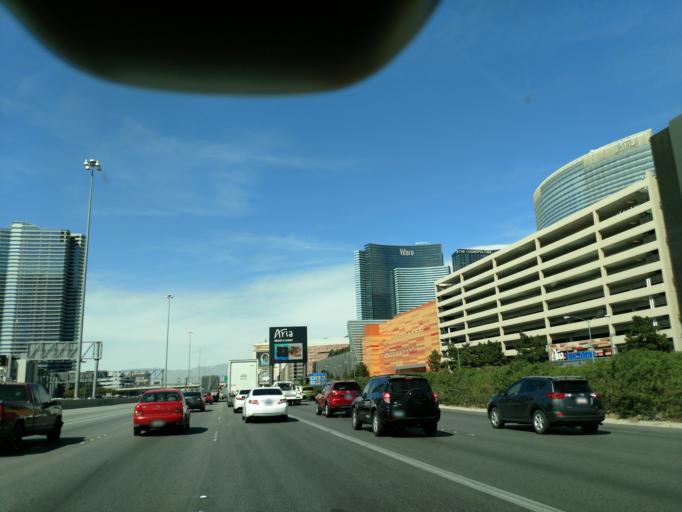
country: US
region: Nevada
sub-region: Clark County
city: Paradise
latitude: 36.1037
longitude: -115.1805
